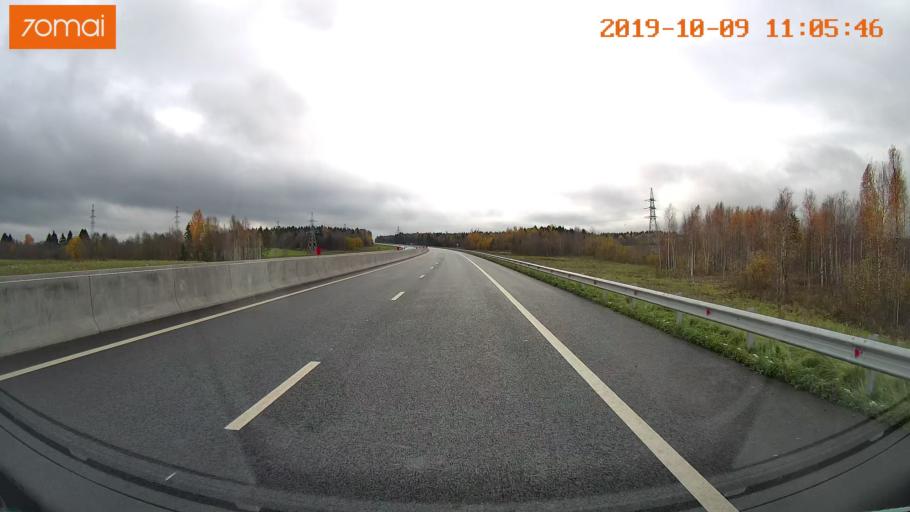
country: RU
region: Vologda
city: Molochnoye
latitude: 59.1953
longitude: 39.7580
